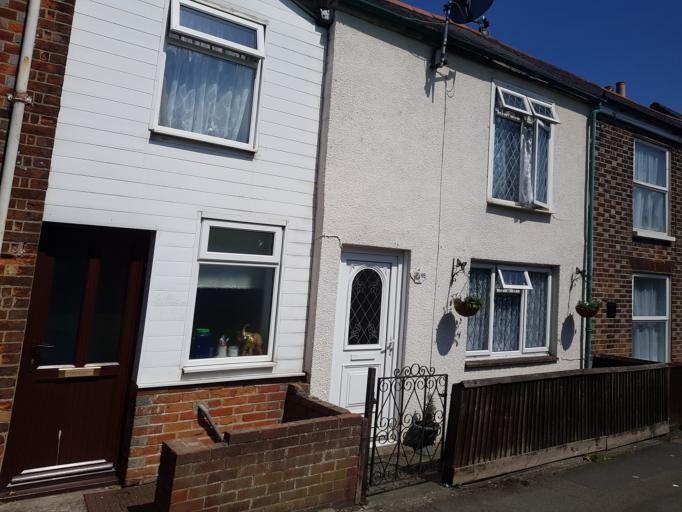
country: GB
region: England
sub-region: Isle of Wight
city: Newport
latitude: 50.7060
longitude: -1.2992
